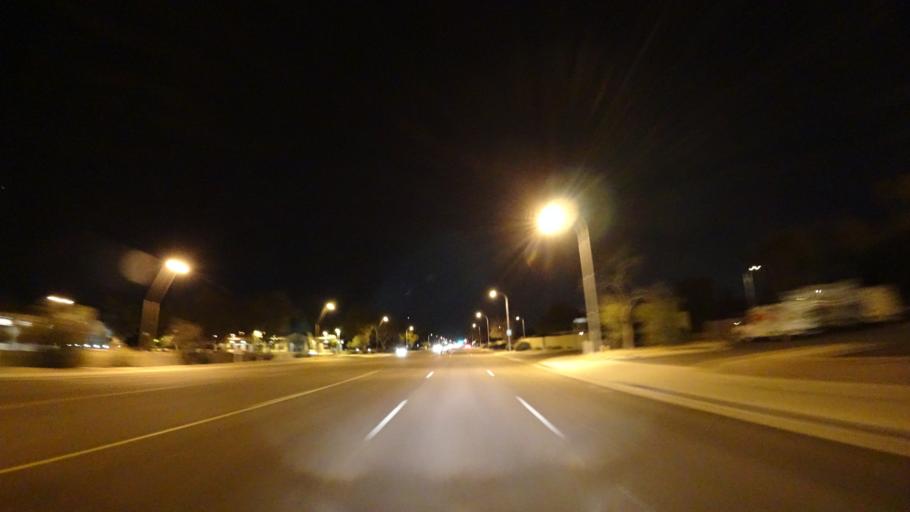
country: US
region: Arizona
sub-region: Maricopa County
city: Tempe
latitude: 33.3786
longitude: -111.8947
